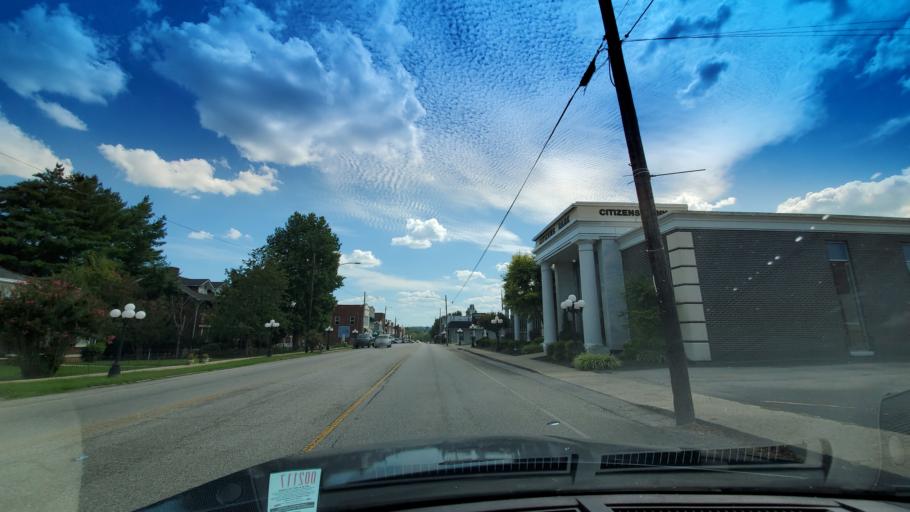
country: US
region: Tennessee
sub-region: Smith County
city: Carthage
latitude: 36.2537
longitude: -85.9518
